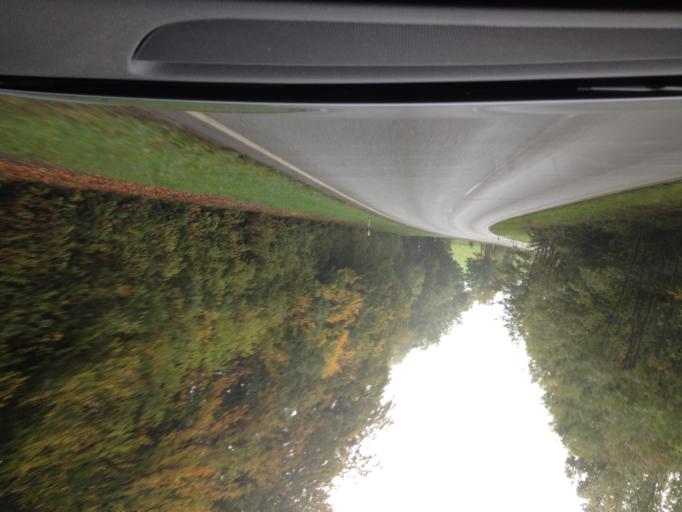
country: DE
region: Baden-Wuerttemberg
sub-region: Regierungsbezirk Stuttgart
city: Bad Rappenau
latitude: 49.2191
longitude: 9.1164
